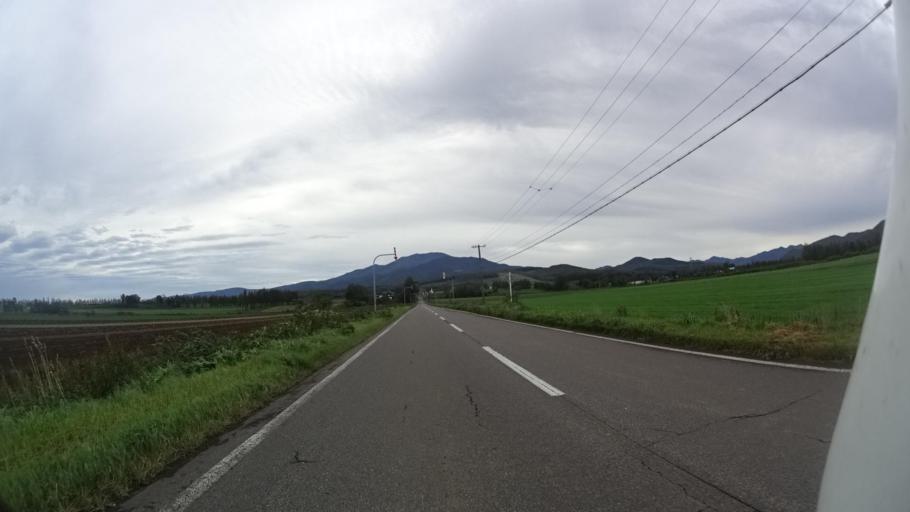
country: JP
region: Hokkaido
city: Shibetsu
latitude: 43.8741
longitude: 144.7393
